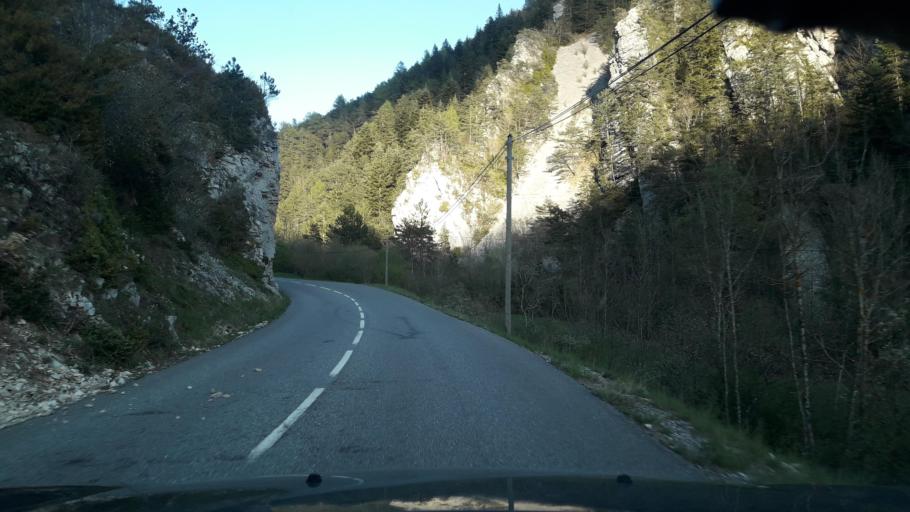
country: FR
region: Rhone-Alpes
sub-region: Departement de l'Isere
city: Mens
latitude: 44.6942
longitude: 5.6092
